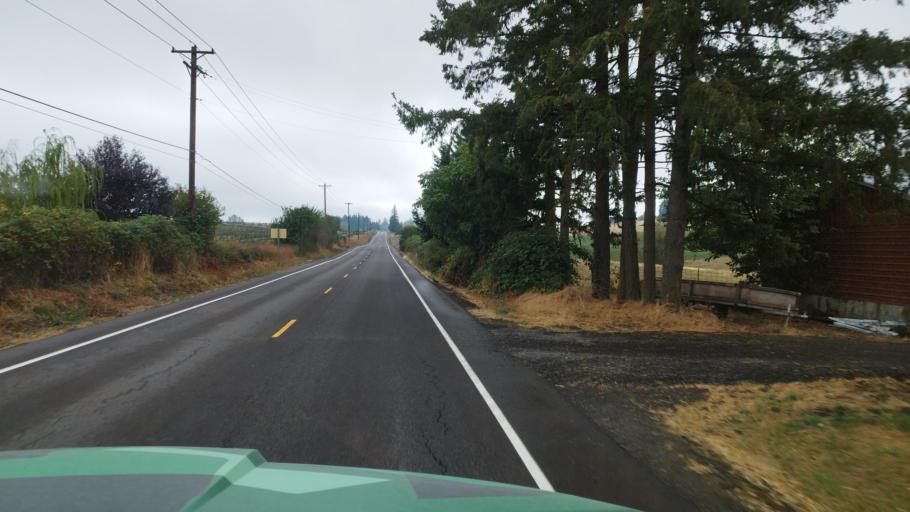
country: US
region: Oregon
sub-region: Yamhill County
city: Yamhill
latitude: 45.3279
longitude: -123.1818
